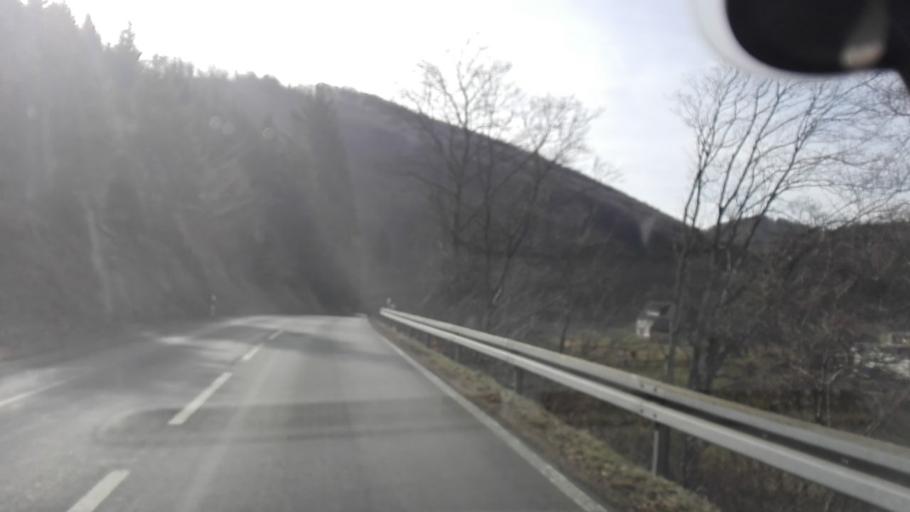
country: DE
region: North Rhine-Westphalia
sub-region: Regierungsbezirk Arnsberg
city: Bad Fredeburg
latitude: 51.1685
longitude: 8.3970
